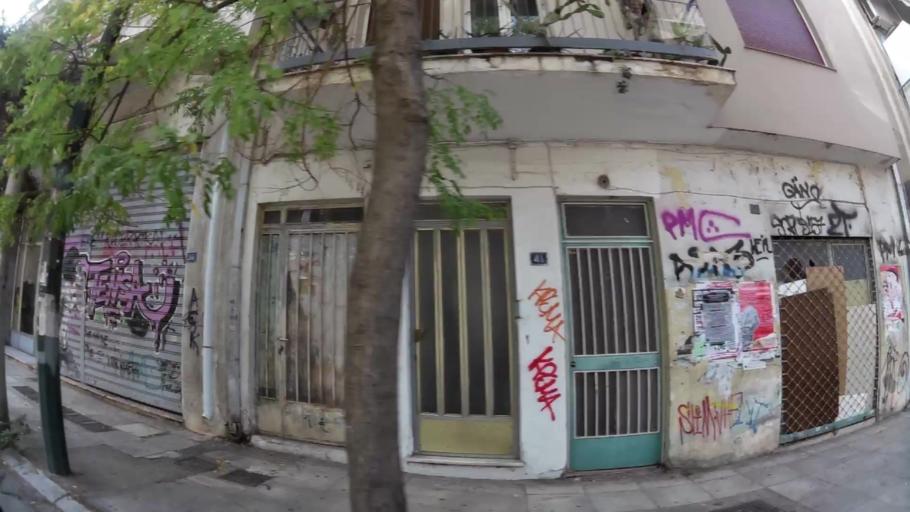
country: GR
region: Attica
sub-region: Nomarchia Athinas
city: Athens
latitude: 37.9647
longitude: 23.7159
